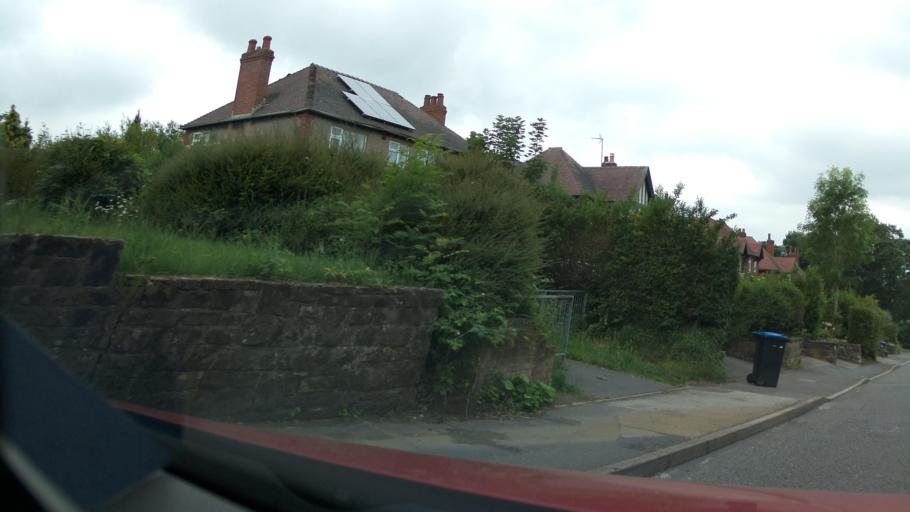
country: GB
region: England
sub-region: Derbyshire
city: Ashbourne
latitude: 53.0109
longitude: -1.7227
